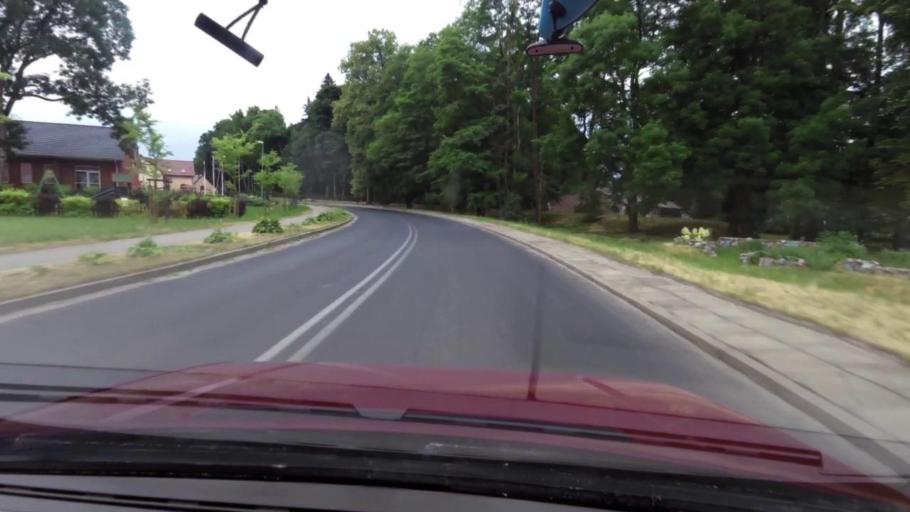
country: PL
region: West Pomeranian Voivodeship
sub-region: Powiat koszalinski
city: Polanow
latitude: 54.1413
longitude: 16.5237
